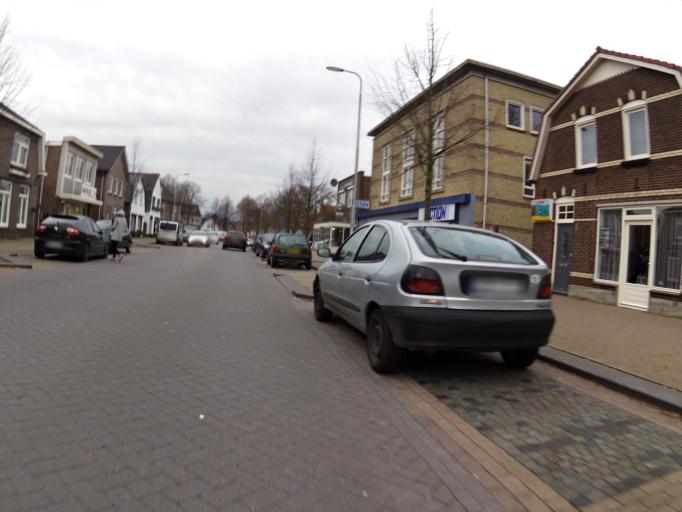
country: NL
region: North Brabant
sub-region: Gemeente Oss
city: Oss
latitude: 51.7597
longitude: 5.5329
